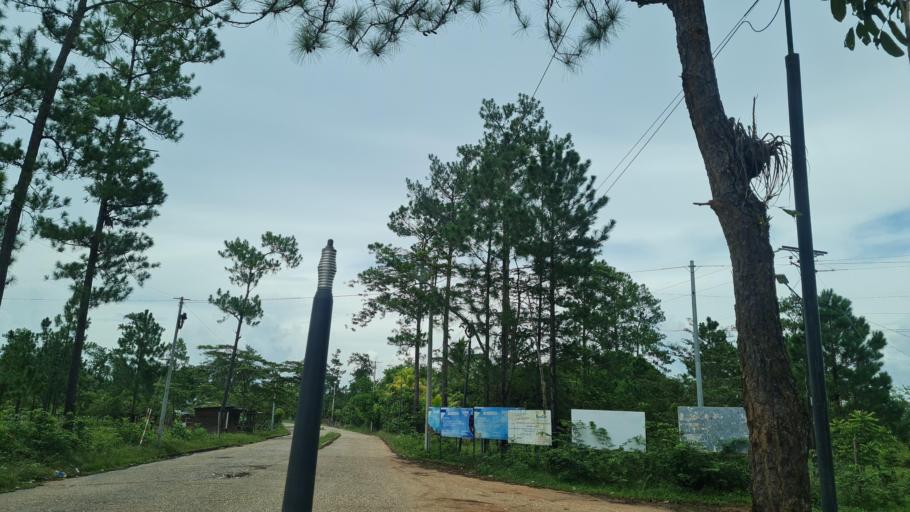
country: NI
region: Atlantico Norte (RAAN)
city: Waspam
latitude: 14.7263
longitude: -83.9719
